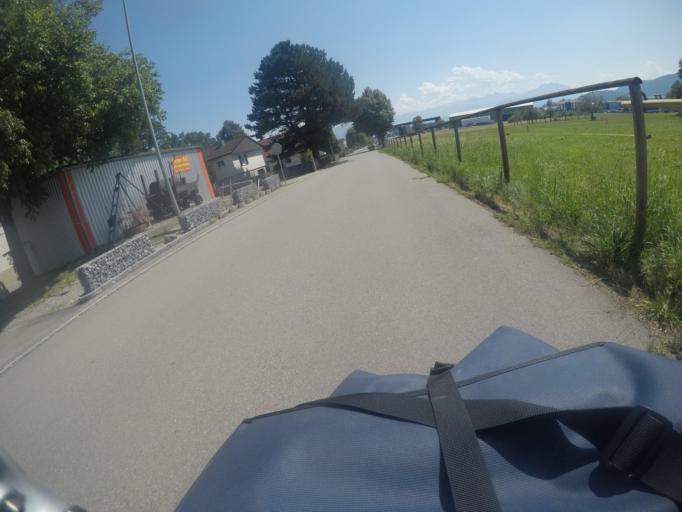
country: CH
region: Saint Gallen
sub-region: Wahlkreis Rheintal
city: Altstatten
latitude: 47.3709
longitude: 9.5572
